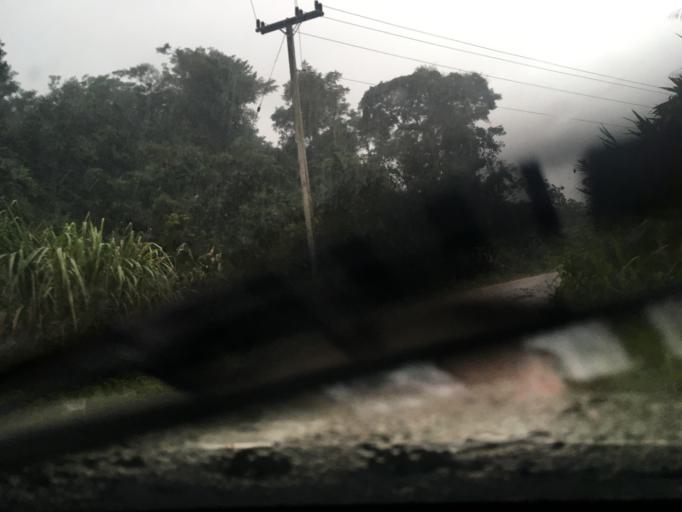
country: LA
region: Oudomxai
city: Muang La
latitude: 21.2273
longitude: 101.9610
